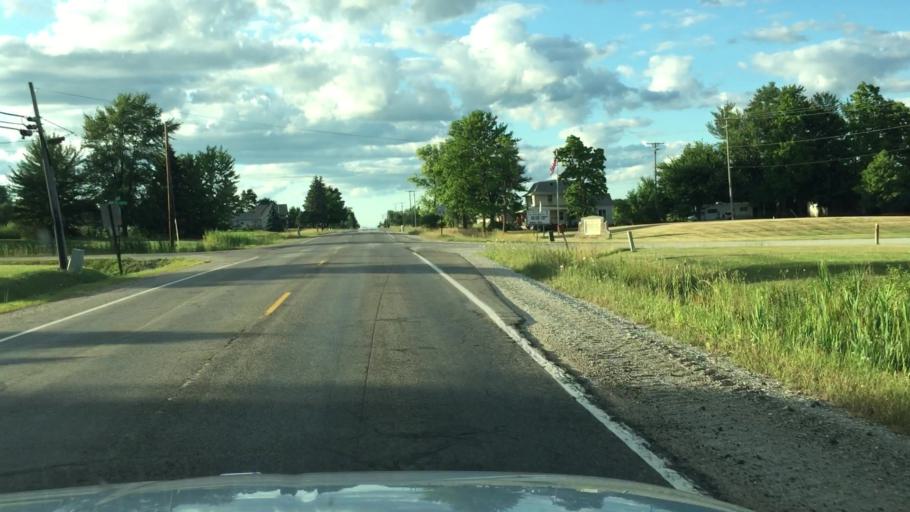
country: US
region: Michigan
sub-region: Saint Clair County
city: Capac
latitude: 43.0267
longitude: -82.9289
